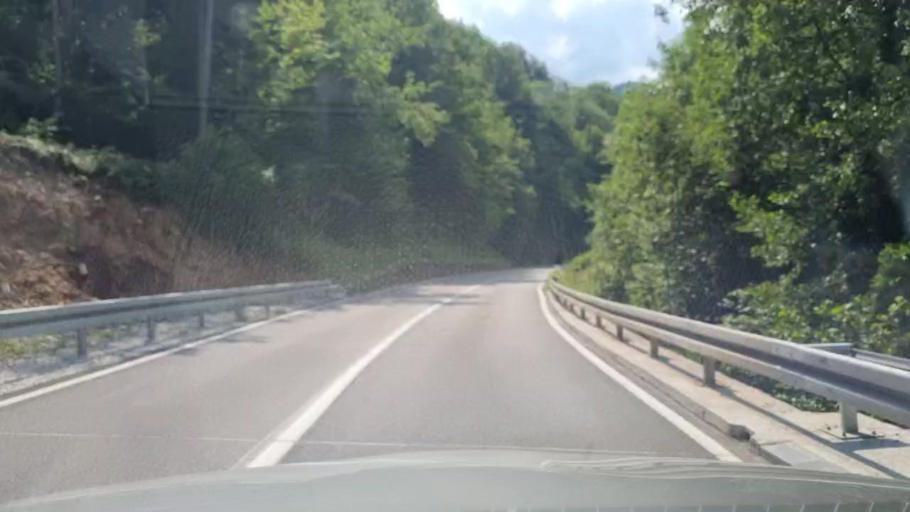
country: BA
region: Republika Srpska
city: Sekovici
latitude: 44.2114
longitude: 18.8026
